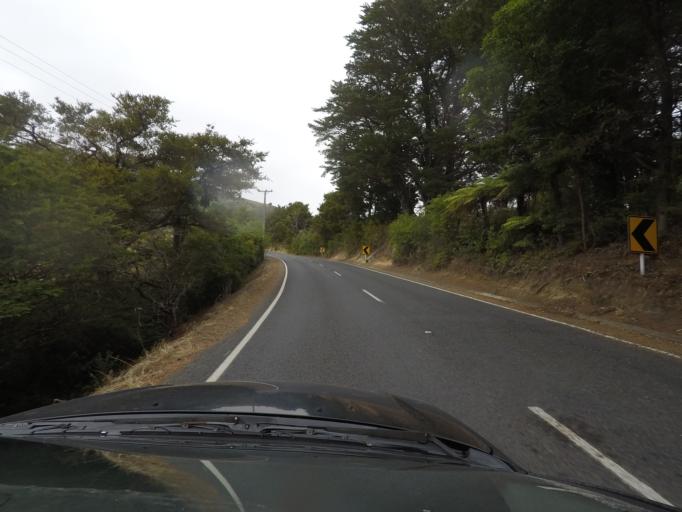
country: NZ
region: Auckland
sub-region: Auckland
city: Warkworth
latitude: -36.2651
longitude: 174.7180
